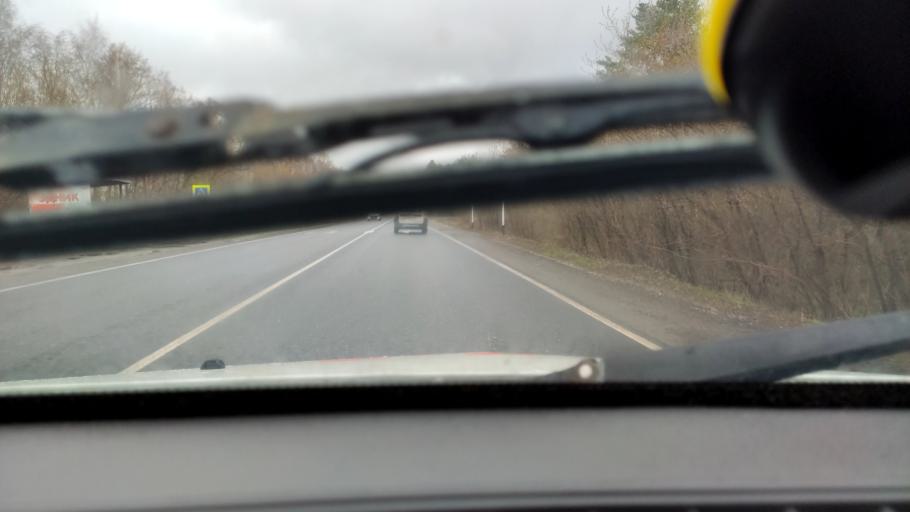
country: RU
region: Samara
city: Povolzhskiy
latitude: 53.6085
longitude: 49.6125
